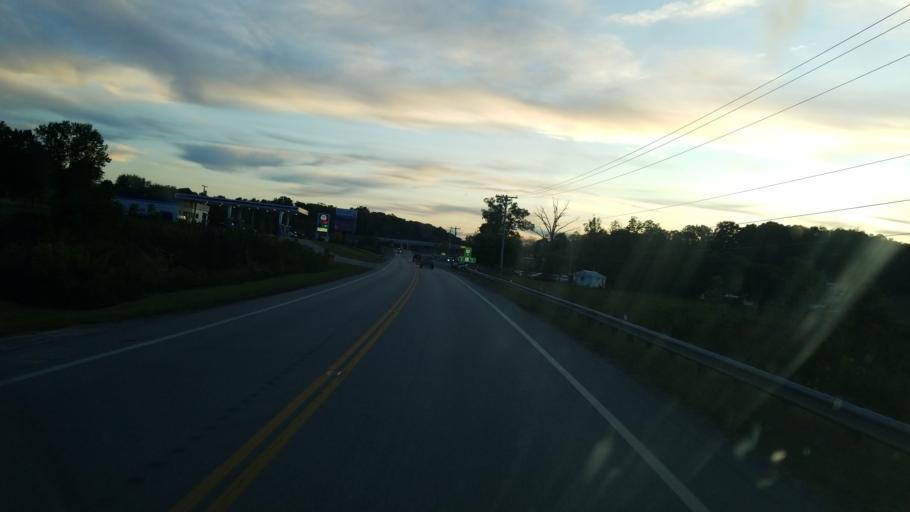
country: US
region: West Virginia
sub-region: Mason County
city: New Haven
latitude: 39.0572
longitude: -81.9689
